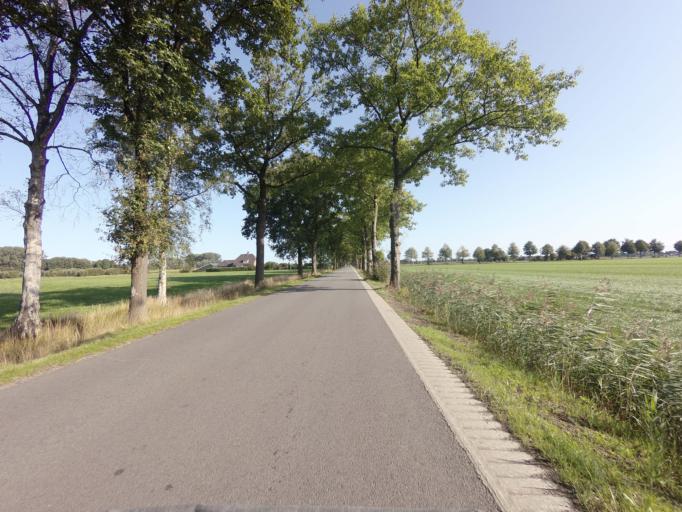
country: NL
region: Overijssel
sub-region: Gemeente Raalte
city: Raalte
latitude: 52.4041
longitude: 6.2838
